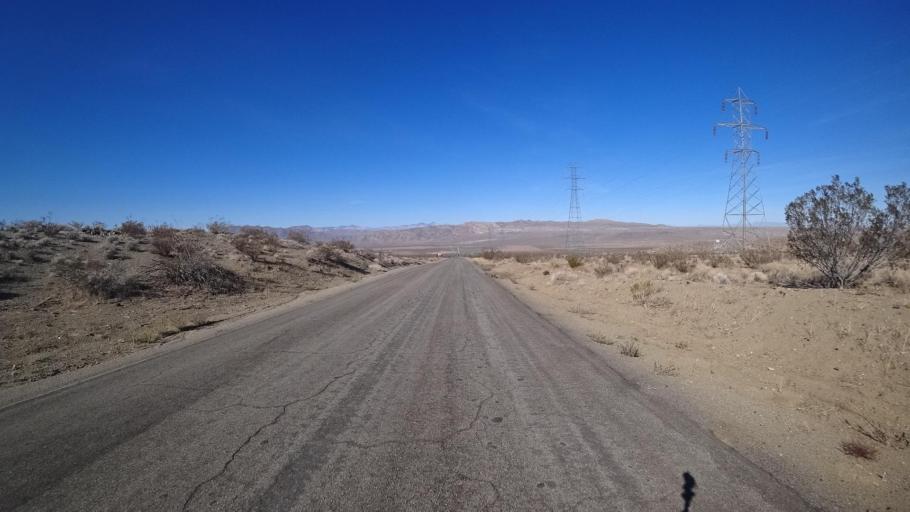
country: US
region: California
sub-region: Kern County
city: Ridgecrest
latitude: 35.3763
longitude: -117.6564
